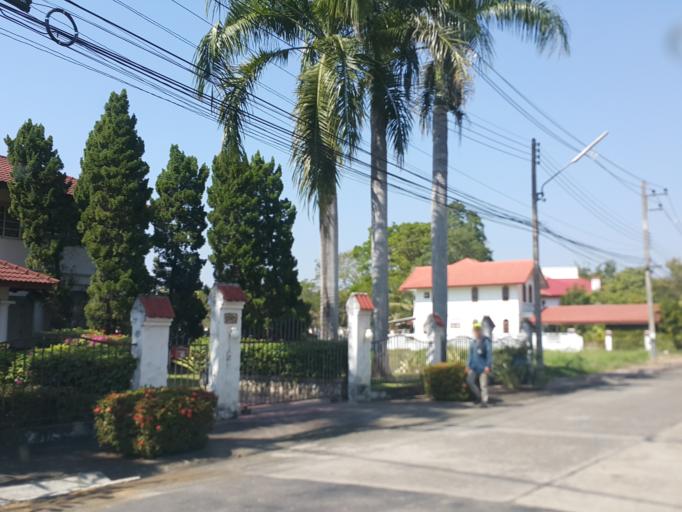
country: TH
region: Chiang Mai
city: Saraphi
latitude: 18.7584
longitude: 99.0235
